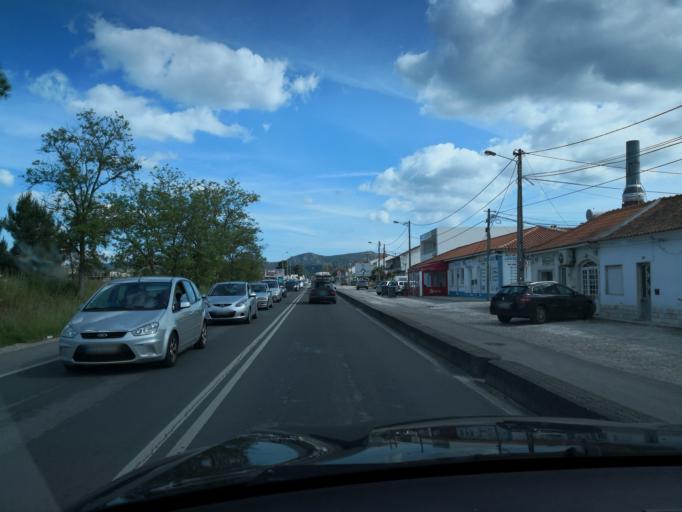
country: PT
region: Setubal
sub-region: Palmela
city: Quinta do Anjo
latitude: 38.5374
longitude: -9.0248
